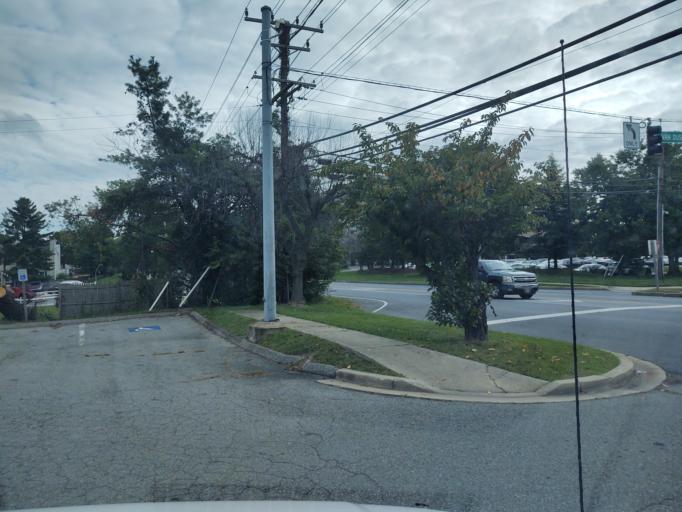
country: US
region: Maryland
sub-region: Prince George's County
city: Laurel
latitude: 39.1043
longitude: -76.8709
